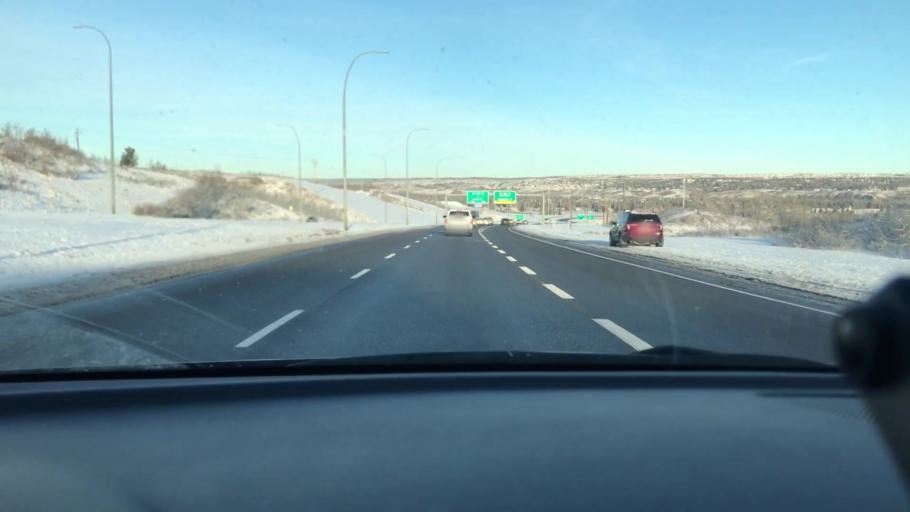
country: CA
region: Alberta
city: Calgary
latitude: 51.0730
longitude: -114.1843
